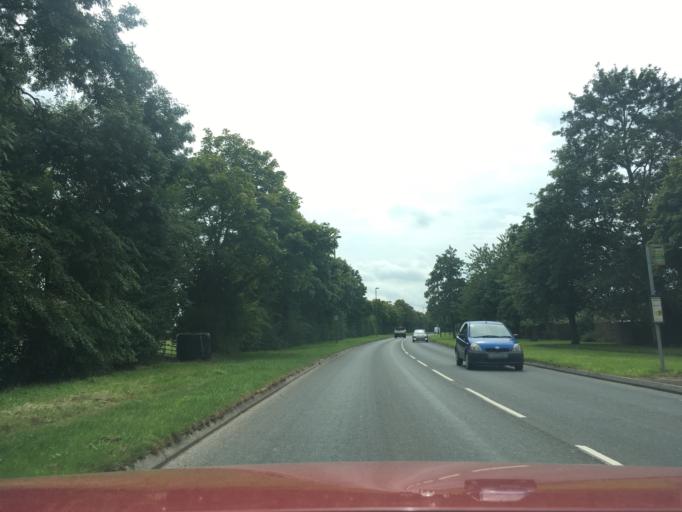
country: GB
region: England
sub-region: South Gloucestershire
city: Thornbury
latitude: 51.6083
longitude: -2.5045
